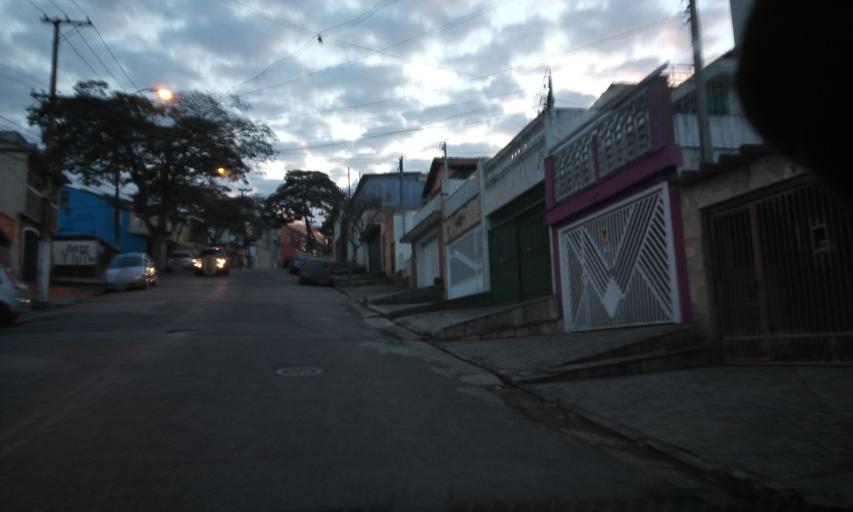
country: BR
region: Sao Paulo
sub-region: Sao Bernardo Do Campo
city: Sao Bernardo do Campo
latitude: -23.6938
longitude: -46.5665
